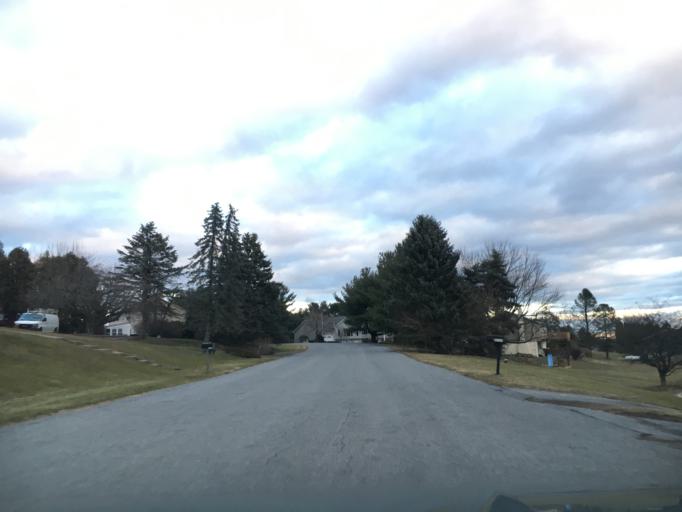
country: US
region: Pennsylvania
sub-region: Lehigh County
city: Schnecksville
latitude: 40.7022
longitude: -75.5818
